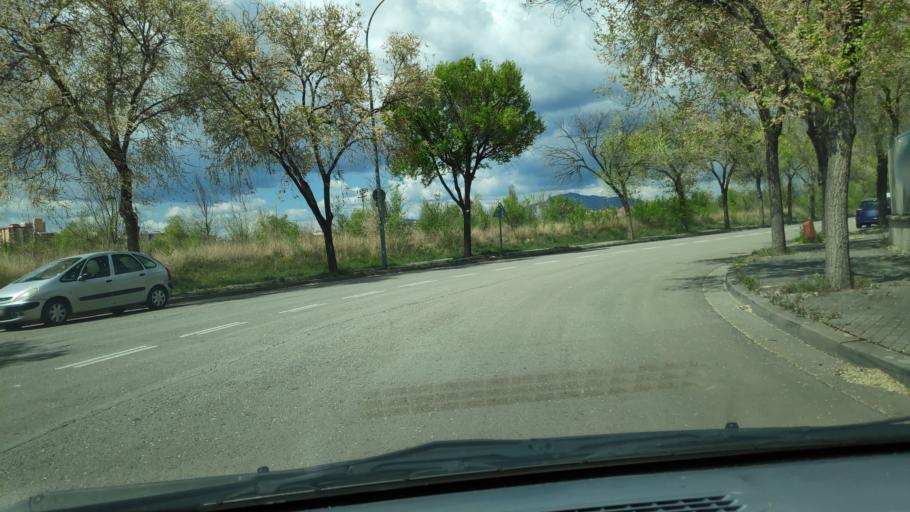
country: ES
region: Catalonia
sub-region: Provincia de Barcelona
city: Barbera del Valles
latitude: 41.5345
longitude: 2.1289
